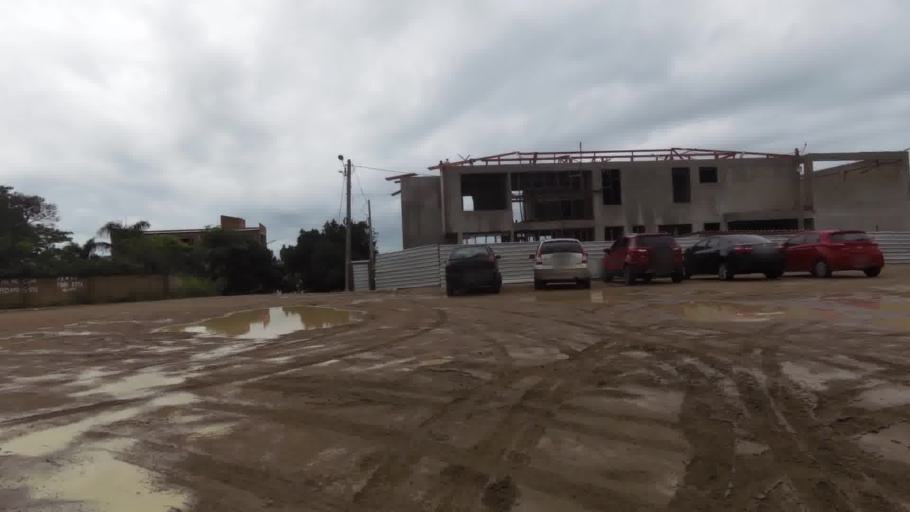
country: BR
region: Espirito Santo
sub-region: Marataizes
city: Marataizes
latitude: -21.0396
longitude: -40.8236
